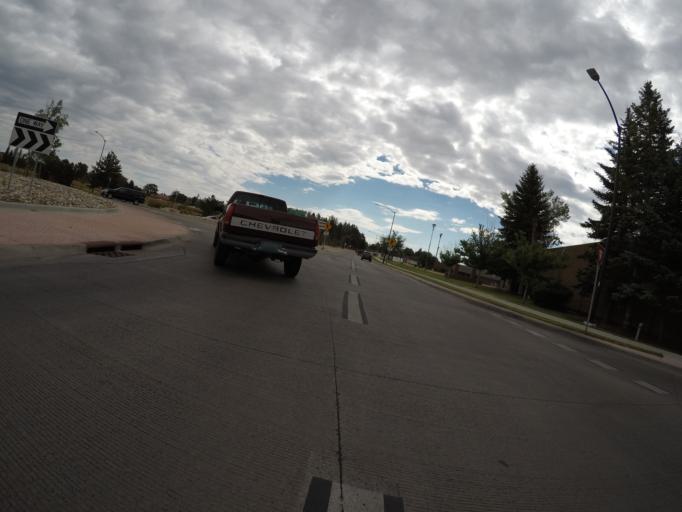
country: US
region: Wyoming
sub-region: Laramie County
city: Cheyenne
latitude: 41.1454
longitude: -104.7899
